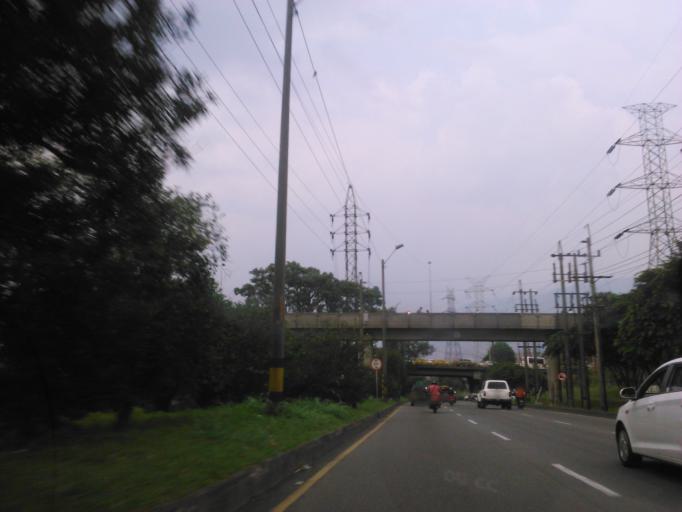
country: CO
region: Antioquia
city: Envigado
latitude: 6.1745
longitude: -75.5965
